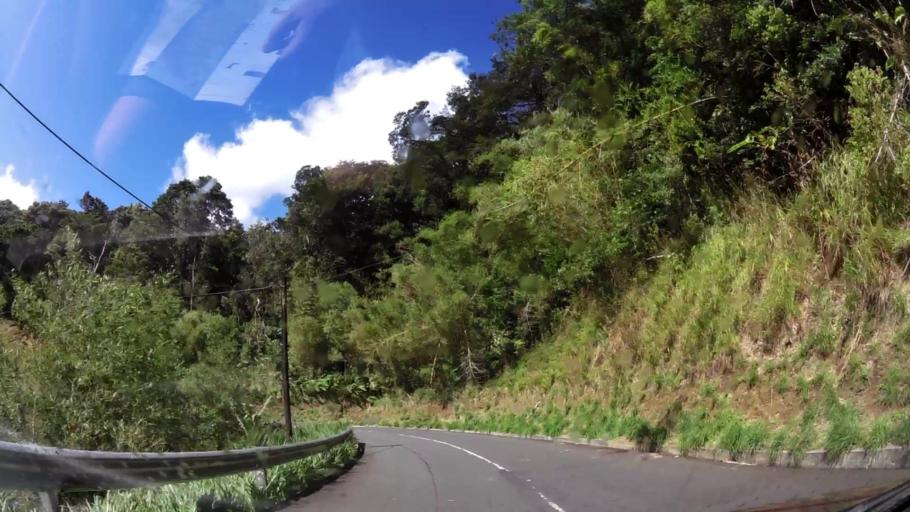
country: DM
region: Saint Paul
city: Pont Casse
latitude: 15.3549
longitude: -61.3580
